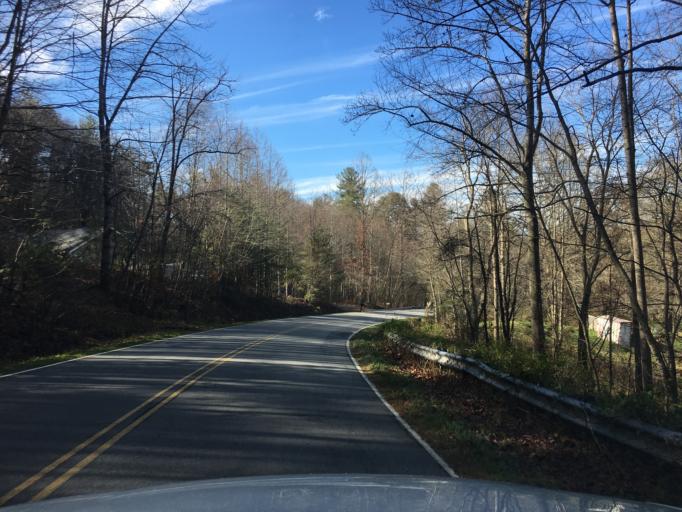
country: US
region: North Carolina
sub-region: Henderson County
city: Etowah
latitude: 35.2314
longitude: -82.5981
